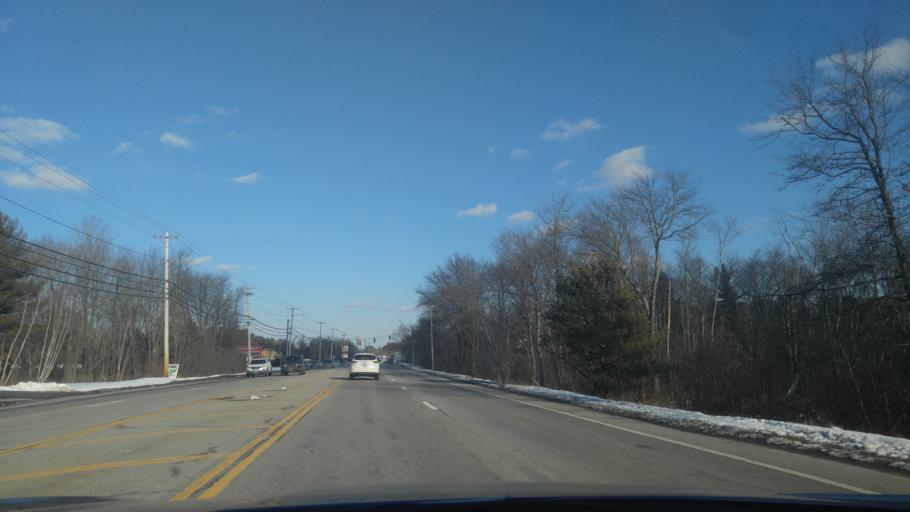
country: US
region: Rhode Island
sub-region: Kent County
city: West Warwick
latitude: 41.6788
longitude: -71.5851
